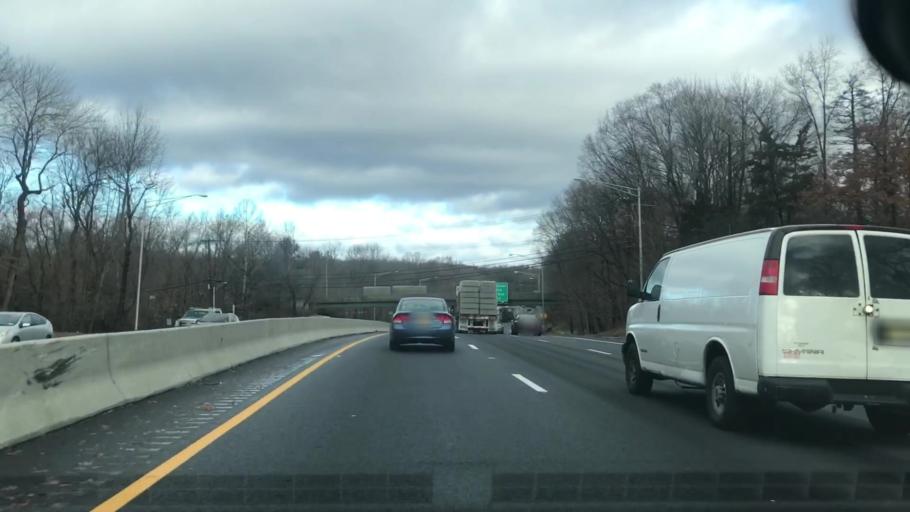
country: US
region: New Jersey
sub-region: Bergen County
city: Ho-Ho-Kus
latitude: 41.0005
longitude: -74.1009
